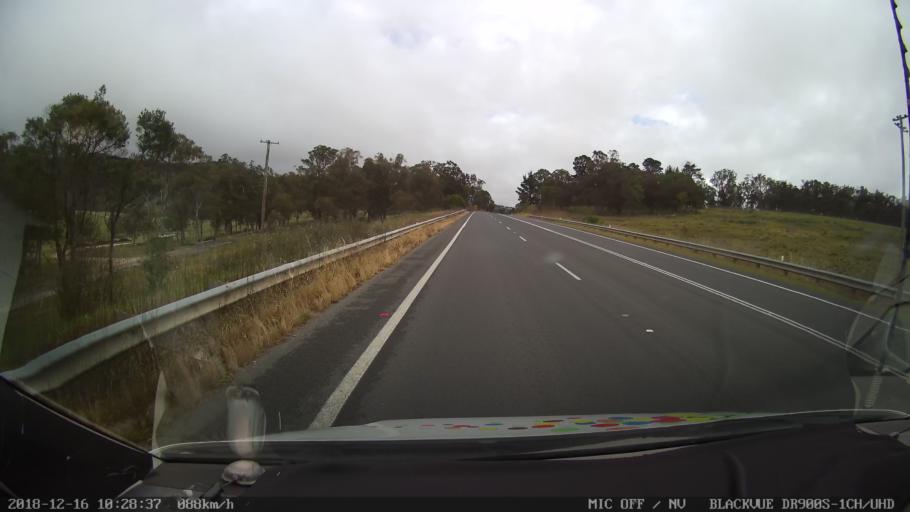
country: AU
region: New South Wales
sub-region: Tenterfield Municipality
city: Carrolls Creek
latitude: -29.1190
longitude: 151.9967
